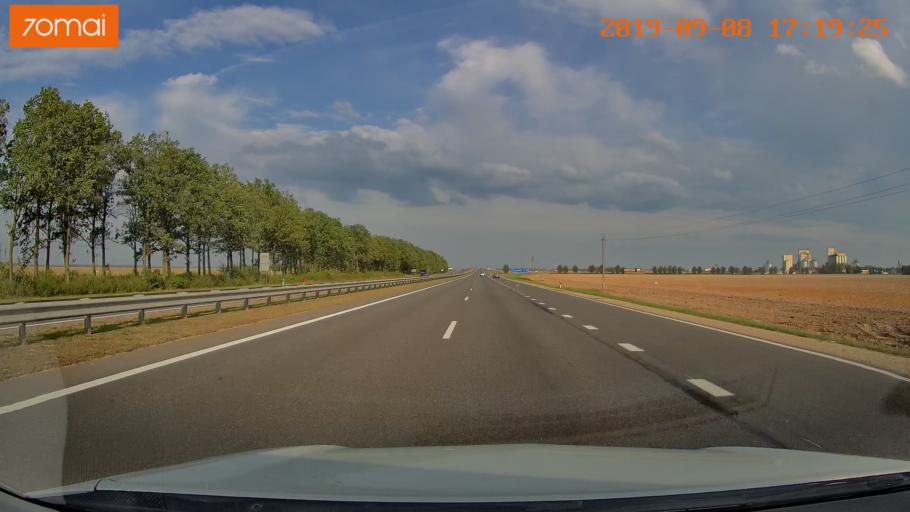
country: BY
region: Grodnenskaya
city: Skidal'
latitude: 53.5844
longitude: 24.1988
